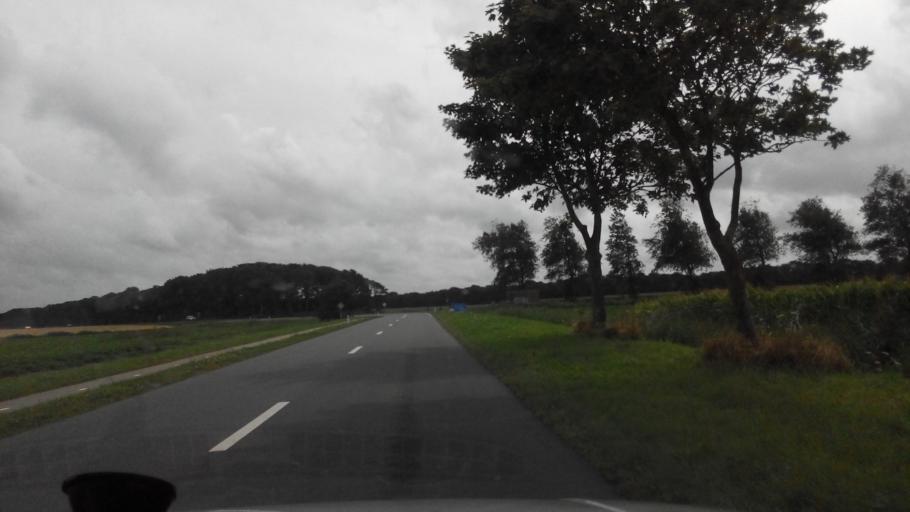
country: NL
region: North Holland
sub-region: Gemeente Hollands Kroon
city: Den Oever
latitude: 52.8832
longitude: 4.9378
